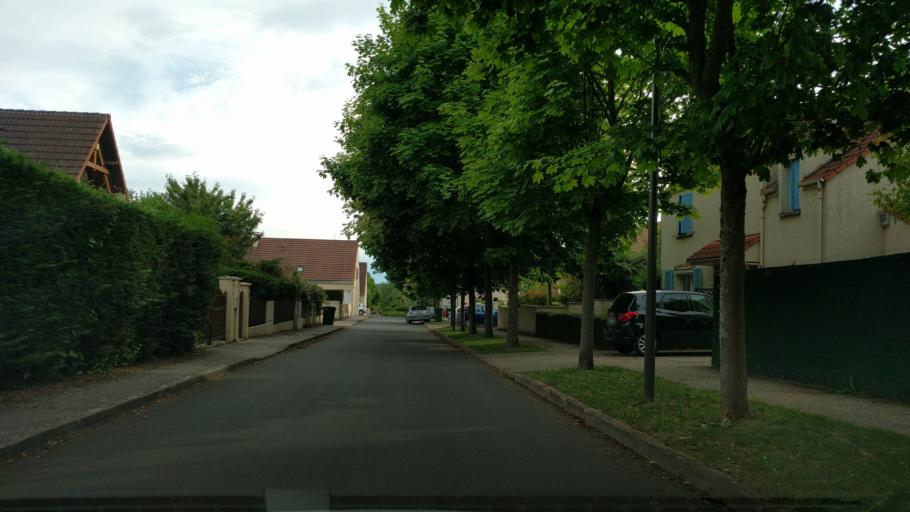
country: FR
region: Ile-de-France
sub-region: Departement de Seine-et-Marne
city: Savigny-le-Temple
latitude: 48.5727
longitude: 2.5890
